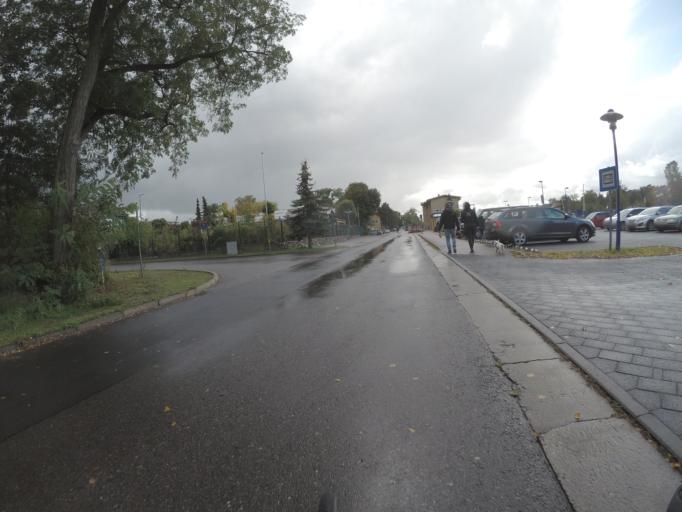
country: DE
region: Brandenburg
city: Wandlitz
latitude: 52.7164
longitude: 13.4342
